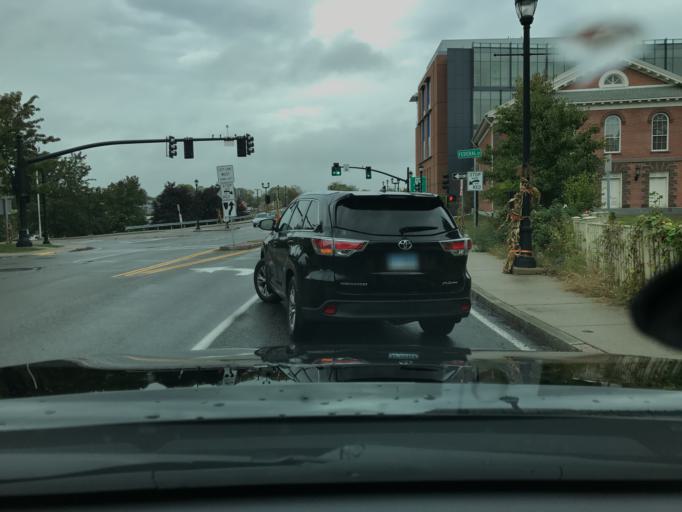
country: US
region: Massachusetts
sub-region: Essex County
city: Salem
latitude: 42.5226
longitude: -70.8987
